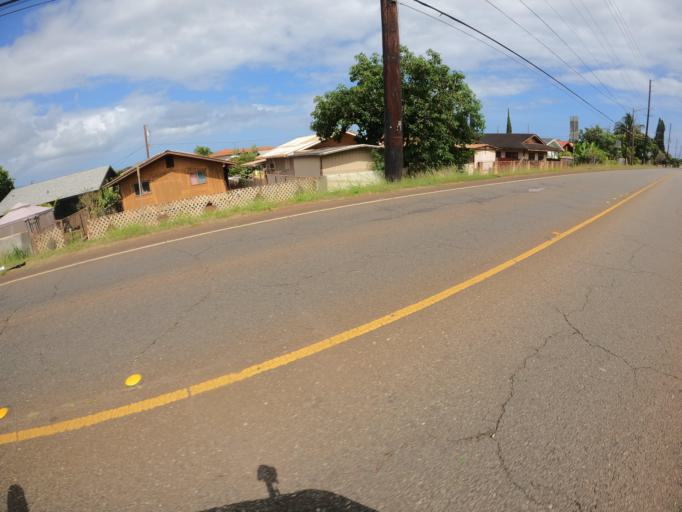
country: US
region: Hawaii
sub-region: Honolulu County
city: Hale'iwa
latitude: 21.5698
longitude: -158.1090
